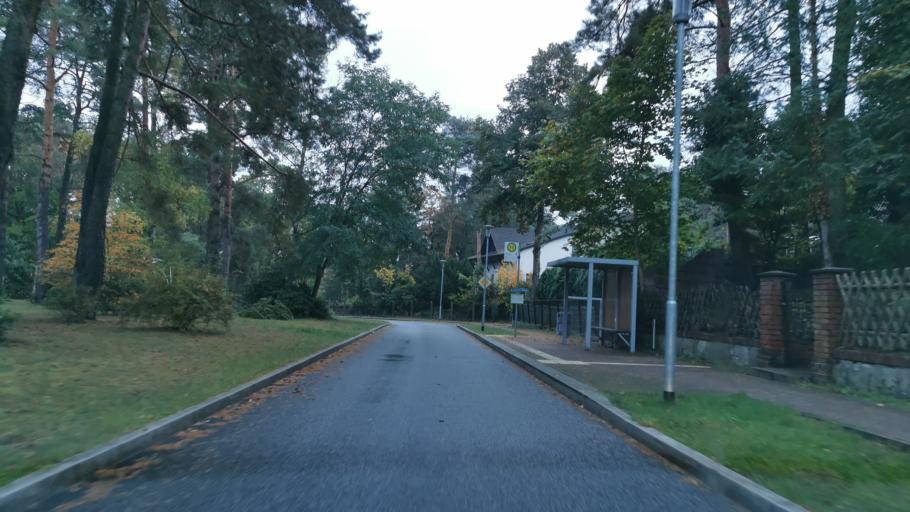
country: DE
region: Brandenburg
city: Michendorf
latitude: 52.3337
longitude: 13.0534
